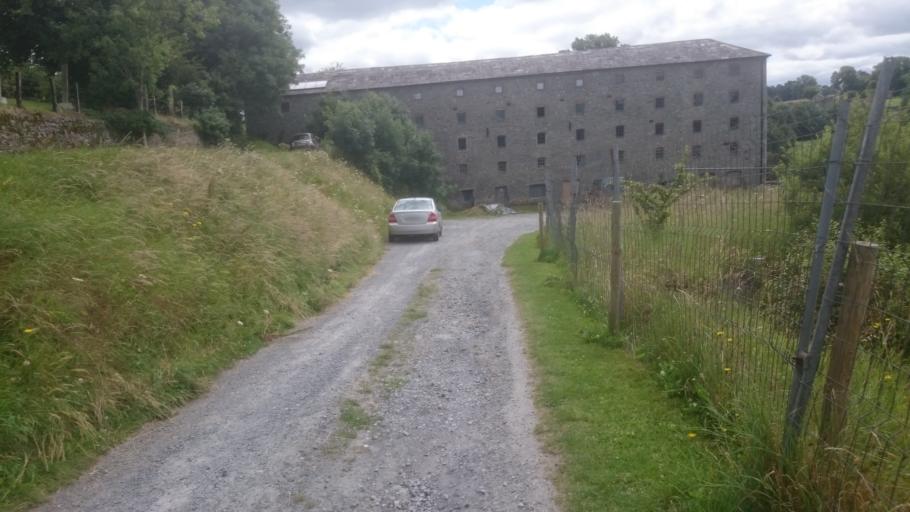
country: IE
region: Leinster
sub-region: Kilkenny
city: Kilkenny
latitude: 52.5416
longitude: -7.2693
